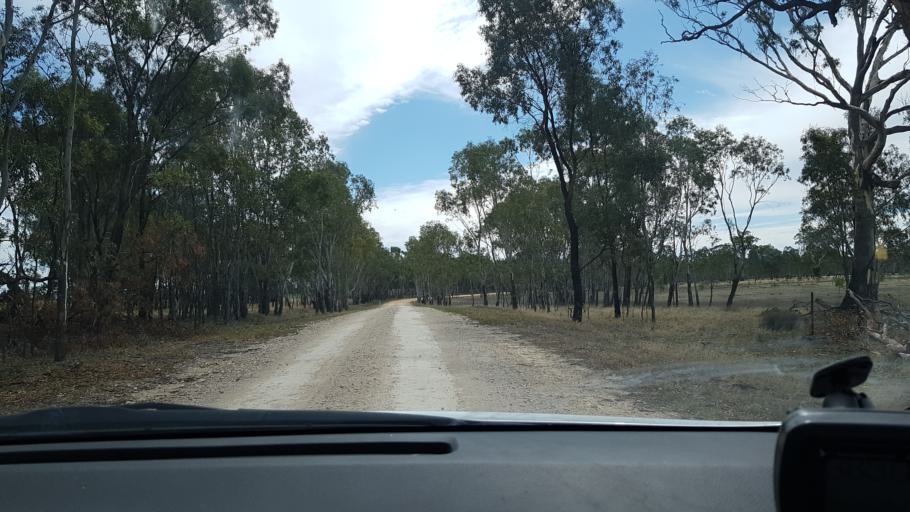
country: AU
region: Victoria
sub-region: Horsham
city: Horsham
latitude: -36.6874
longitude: 141.7814
